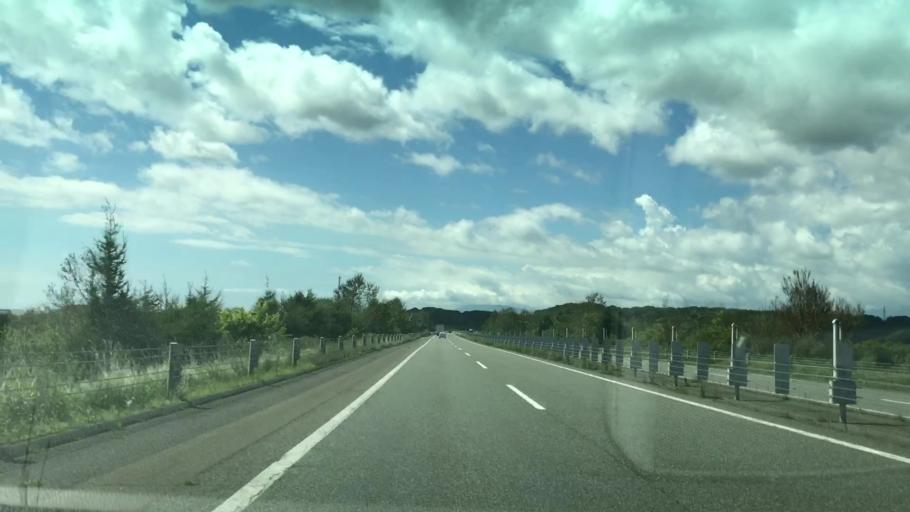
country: JP
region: Hokkaido
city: Shiraoi
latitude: 42.5862
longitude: 141.4165
